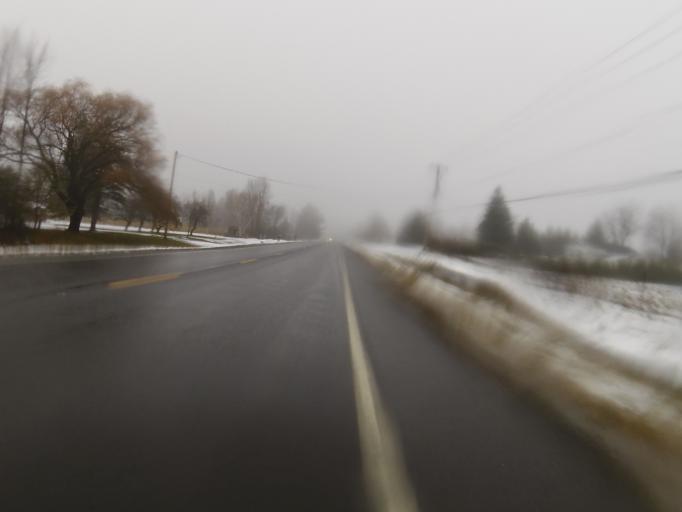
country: CA
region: Ontario
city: Perth
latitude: 44.8150
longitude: -76.3923
